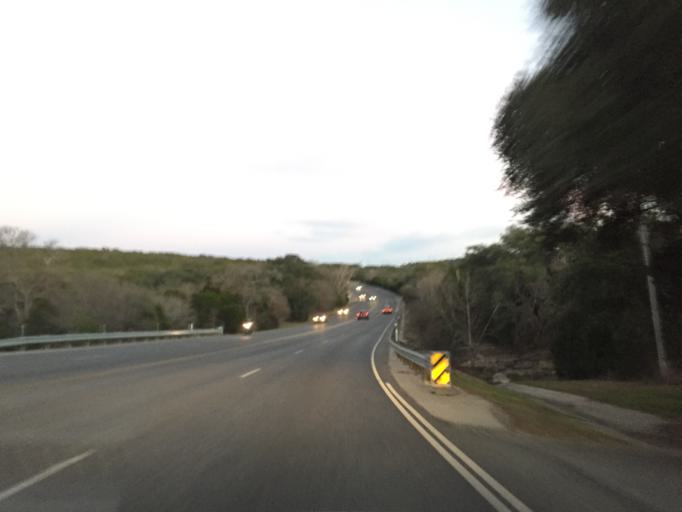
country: US
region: Texas
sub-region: Travis County
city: Jonestown
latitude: 30.5198
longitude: -97.8975
